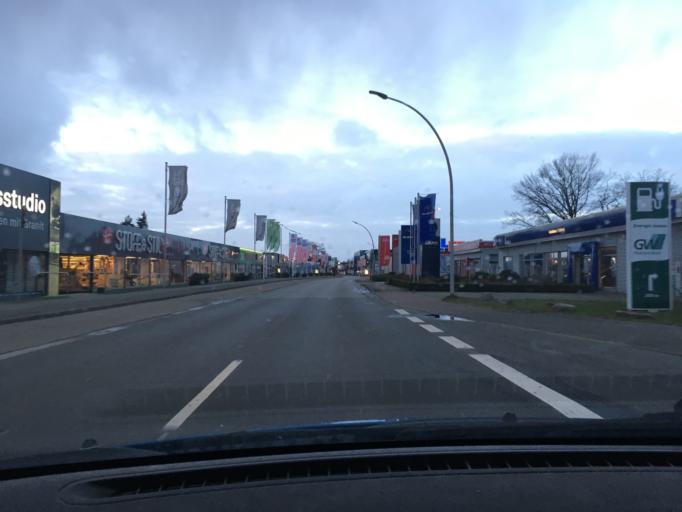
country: DE
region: Schleswig-Holstein
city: Halstenbek
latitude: 53.6291
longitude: 9.8662
